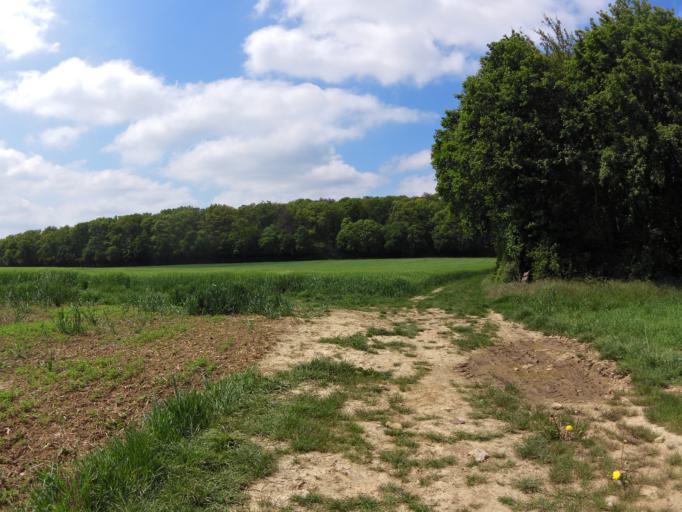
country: DE
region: Bavaria
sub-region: Regierungsbezirk Unterfranken
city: Reichenberg
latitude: 49.7406
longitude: 9.9049
